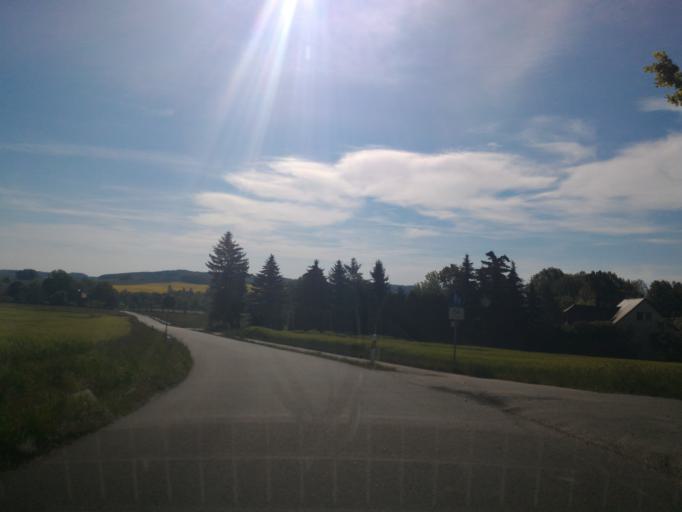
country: DE
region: Saxony
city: Niedercunnersdorf
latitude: 51.0533
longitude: 14.6460
